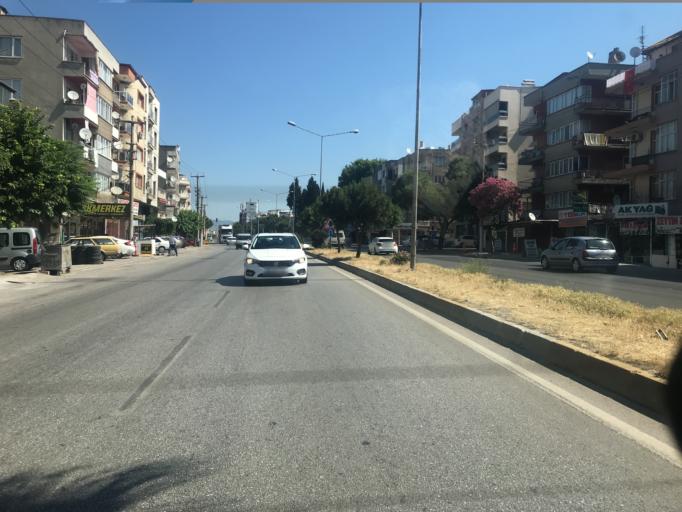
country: TR
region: Manisa
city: Akhisar
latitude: 38.9247
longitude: 27.8344
